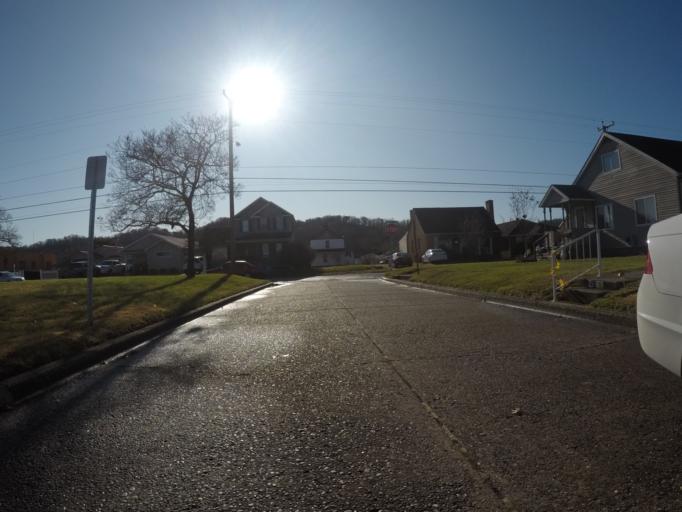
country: US
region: Ohio
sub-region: Lawrence County
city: Burlington
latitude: 38.4024
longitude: -82.5144
